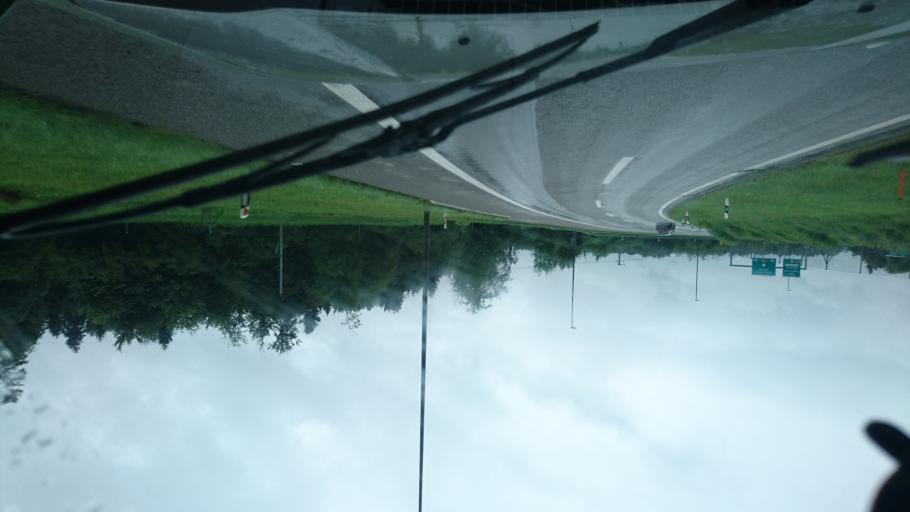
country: CH
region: Zurich
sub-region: Bezirk Hinwil
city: Bubikon
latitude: 47.2907
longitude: 8.8157
